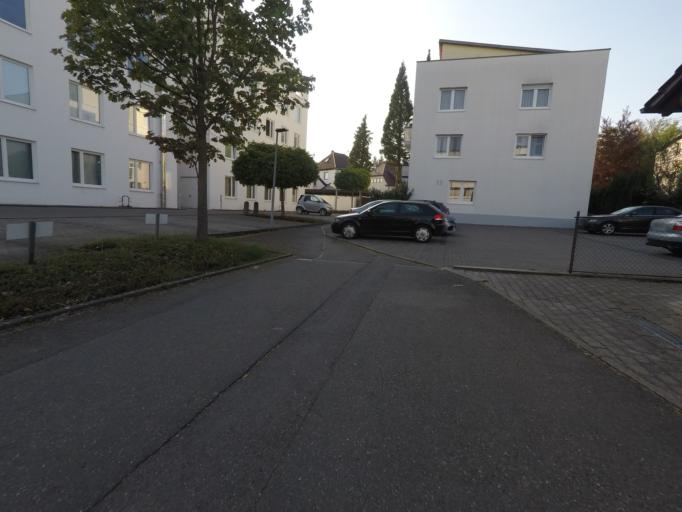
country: DE
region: Baden-Wuerttemberg
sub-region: Tuebingen Region
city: Eningen unter Achalm
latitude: 48.4782
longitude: 9.2510
